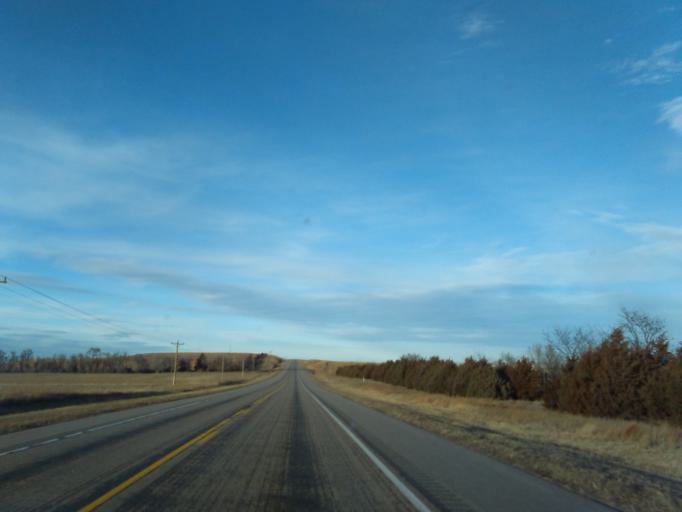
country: US
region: Nebraska
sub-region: Morrill County
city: Bridgeport
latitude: 41.5587
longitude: -102.9846
